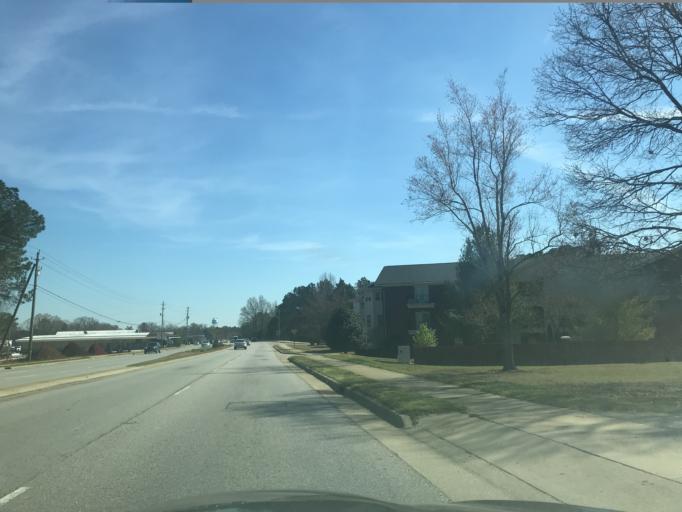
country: US
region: North Carolina
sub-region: Wake County
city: Fuquay-Varina
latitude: 35.6018
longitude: -78.8028
